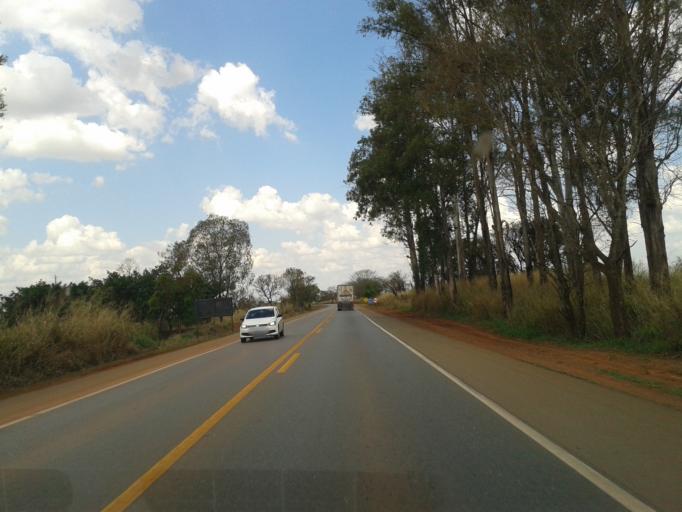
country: BR
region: Minas Gerais
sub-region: Luz
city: Luz
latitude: -19.7837
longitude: -45.7205
